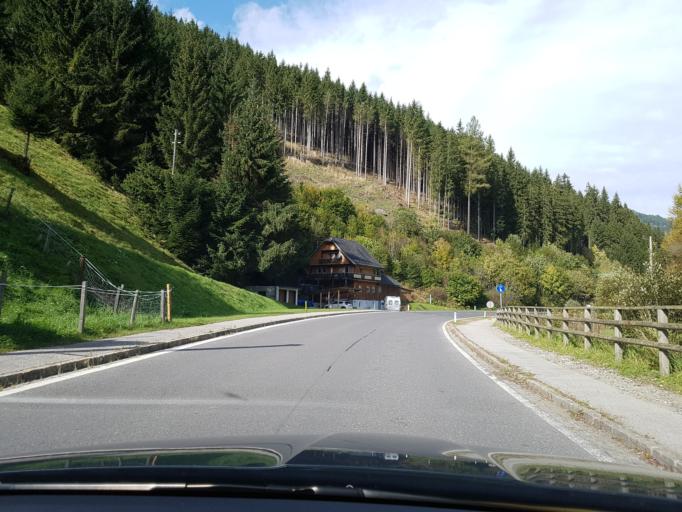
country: AT
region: Carinthia
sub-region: Politischer Bezirk Spittal an der Drau
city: Kleinkirchheim
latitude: 46.8582
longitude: 13.8916
